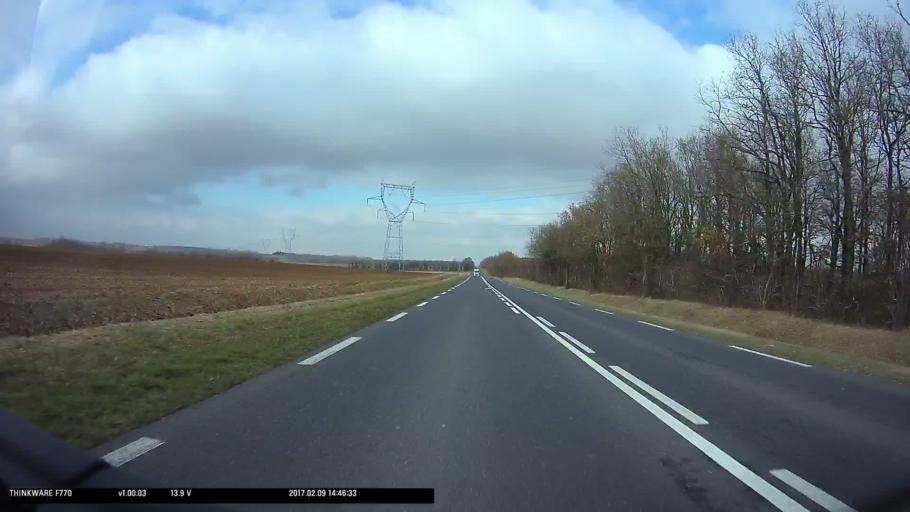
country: FR
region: Centre
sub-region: Departement du Cher
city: Trouy
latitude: 46.9859
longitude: 2.3956
